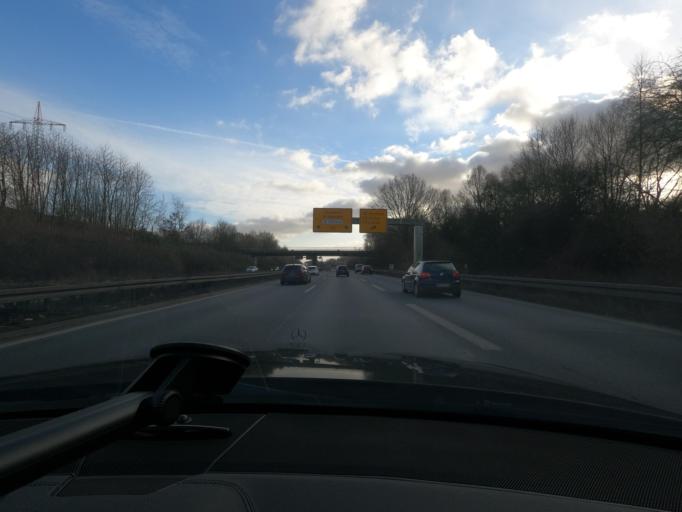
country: DE
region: North Rhine-Westphalia
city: Lunen
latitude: 51.5700
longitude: 7.4997
